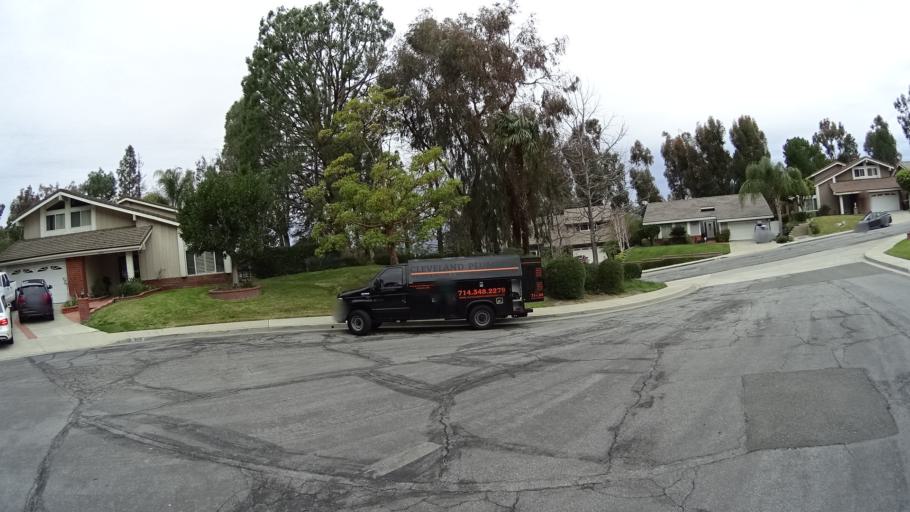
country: US
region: California
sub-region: Orange County
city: Villa Park
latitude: 33.8370
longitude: -117.7624
